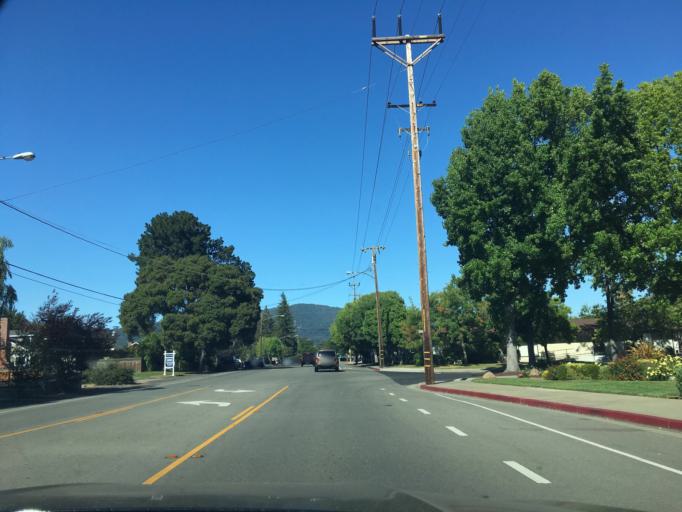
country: US
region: California
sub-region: Santa Clara County
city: Los Gatos
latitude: 37.2416
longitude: -121.9577
